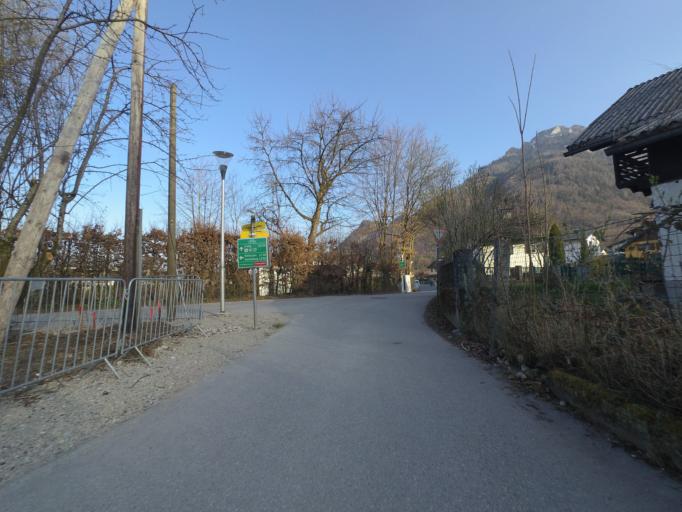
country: AT
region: Salzburg
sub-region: Politischer Bezirk Salzburg-Umgebung
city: Grodig
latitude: 47.7504
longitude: 12.9942
